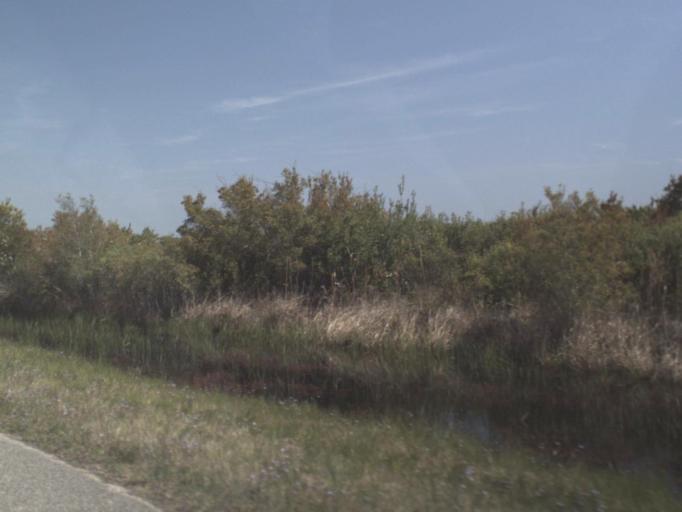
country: US
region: Florida
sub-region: Franklin County
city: Apalachicola
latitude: 29.7249
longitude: -85.0907
